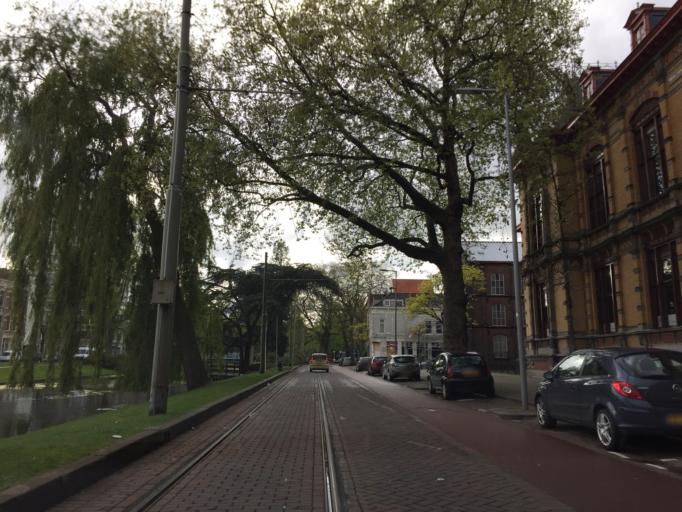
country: NL
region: South Holland
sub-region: Gemeente Rotterdam
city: Rotterdam
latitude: 51.9315
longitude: 4.4766
